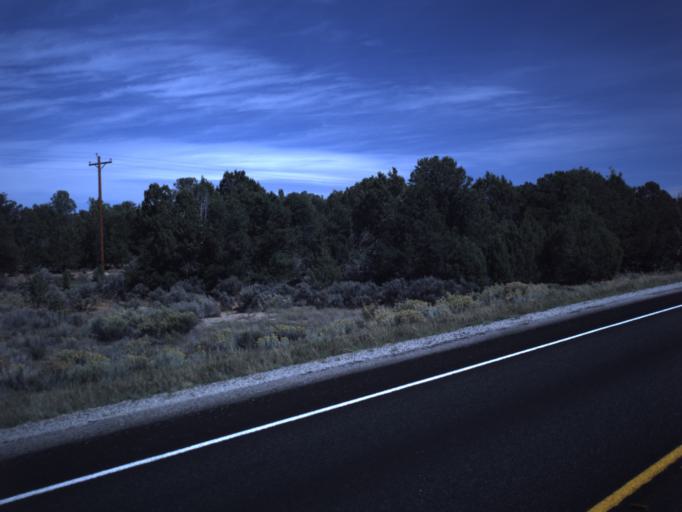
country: US
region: Utah
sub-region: San Juan County
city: Monticello
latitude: 37.8408
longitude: -109.1267
